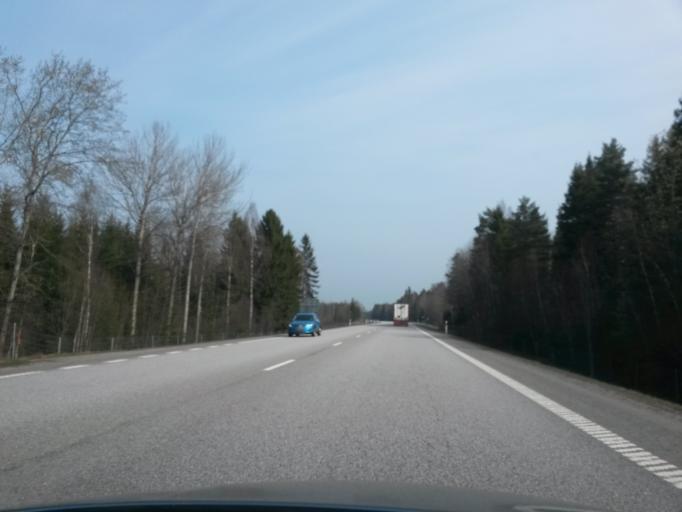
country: SE
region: Vaestra Goetaland
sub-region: Mariestads Kommun
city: Mariestad
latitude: 58.7181
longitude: 13.8810
